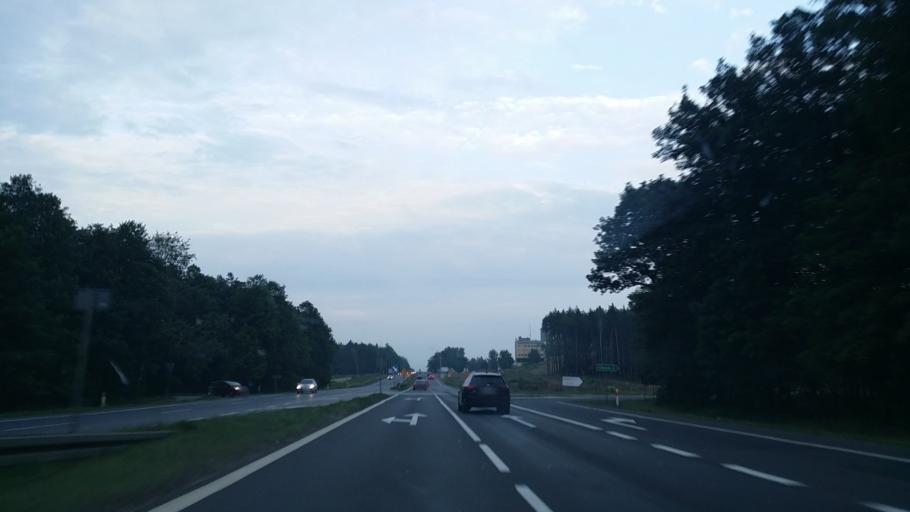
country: PL
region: Lower Silesian Voivodeship
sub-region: Powiat lubinski
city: Lubin
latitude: 51.4406
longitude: 16.1477
